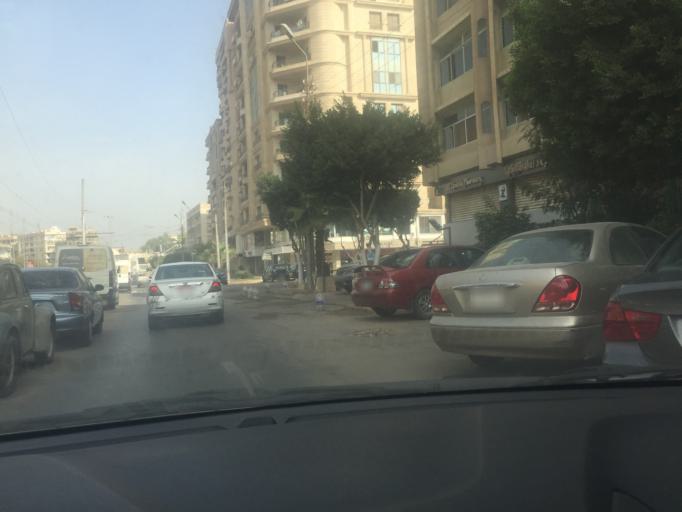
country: EG
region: Muhafazat al Qahirah
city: Cairo
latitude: 30.0835
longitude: 31.3478
